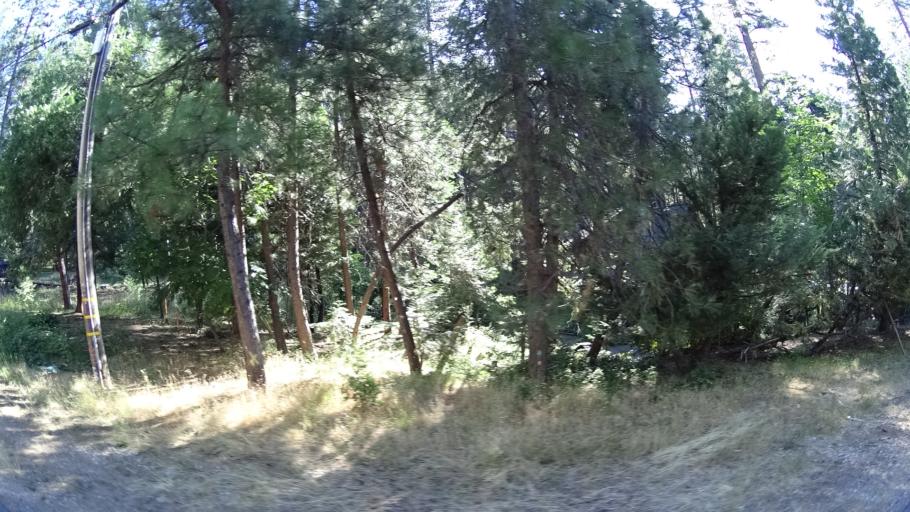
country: US
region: California
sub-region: Calaveras County
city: Arnold
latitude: 38.2630
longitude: -120.3223
